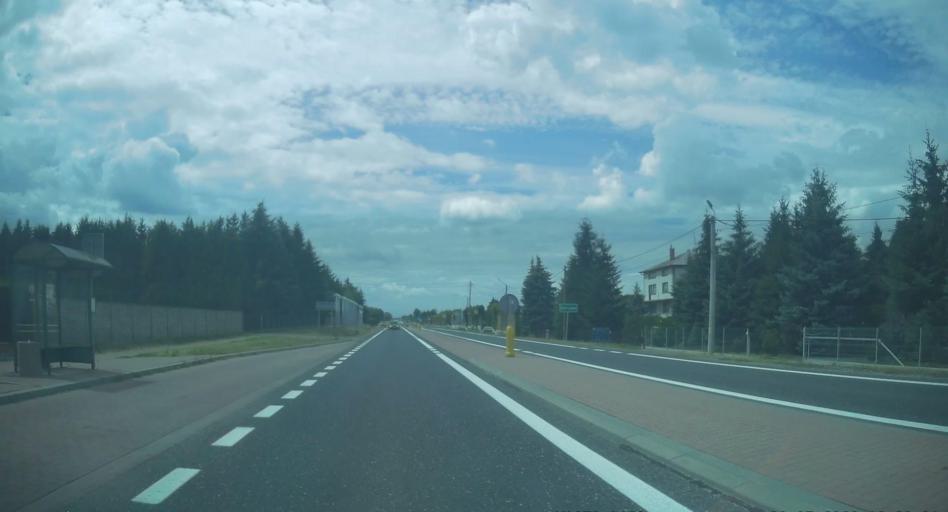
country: PL
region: Subcarpathian Voivodeship
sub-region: Powiat ropczycko-sedziszowski
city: Ostrow
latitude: 50.0621
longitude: 21.5430
